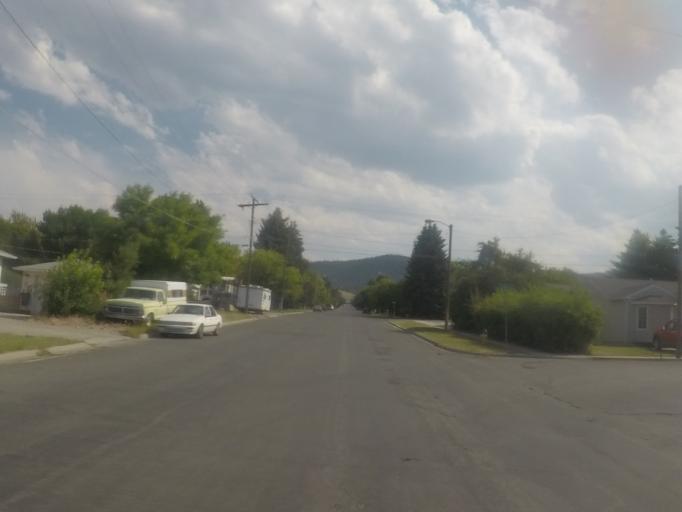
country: US
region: Montana
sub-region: Lewis and Clark County
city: Helena
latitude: 46.5891
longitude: -112.0072
